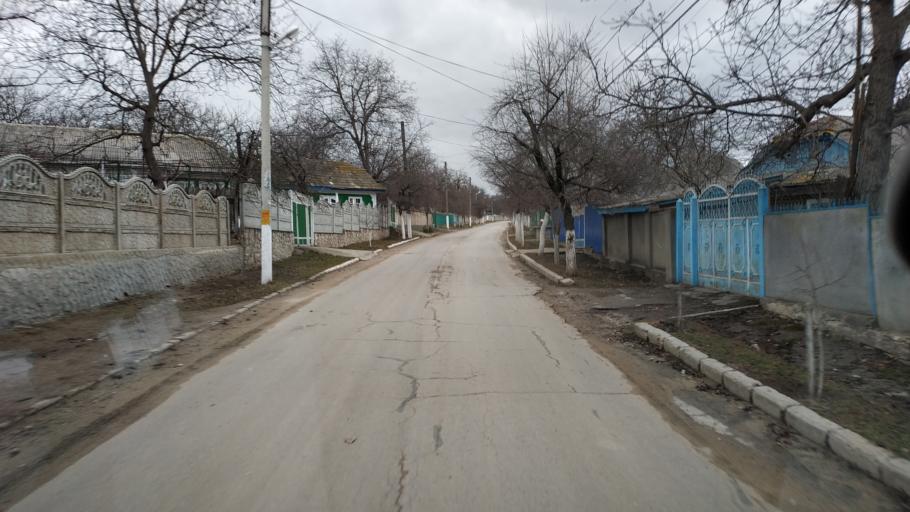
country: MD
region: Calarasi
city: Calarasi
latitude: 47.2590
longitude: 28.1380
